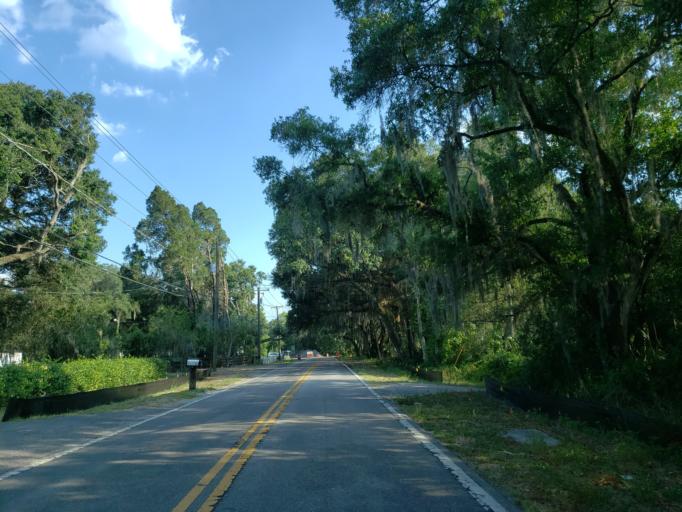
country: US
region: Florida
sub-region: Hillsborough County
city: Fish Hawk
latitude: 27.8441
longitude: -82.2000
